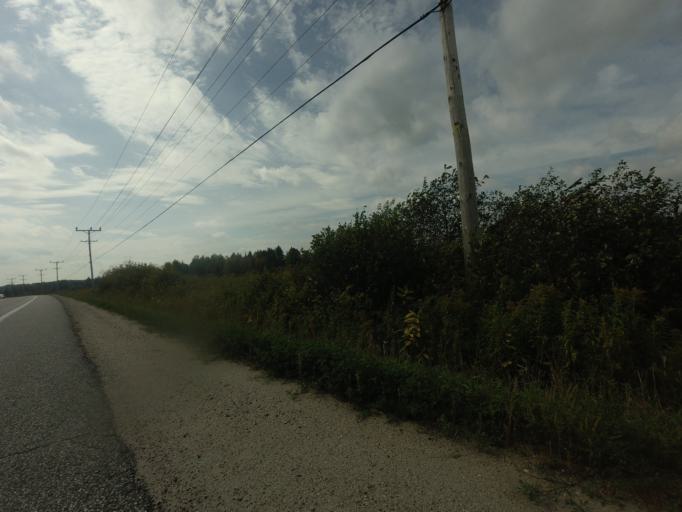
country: CA
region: Quebec
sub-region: Outaouais
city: Wakefield
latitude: 45.8812
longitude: -76.0279
